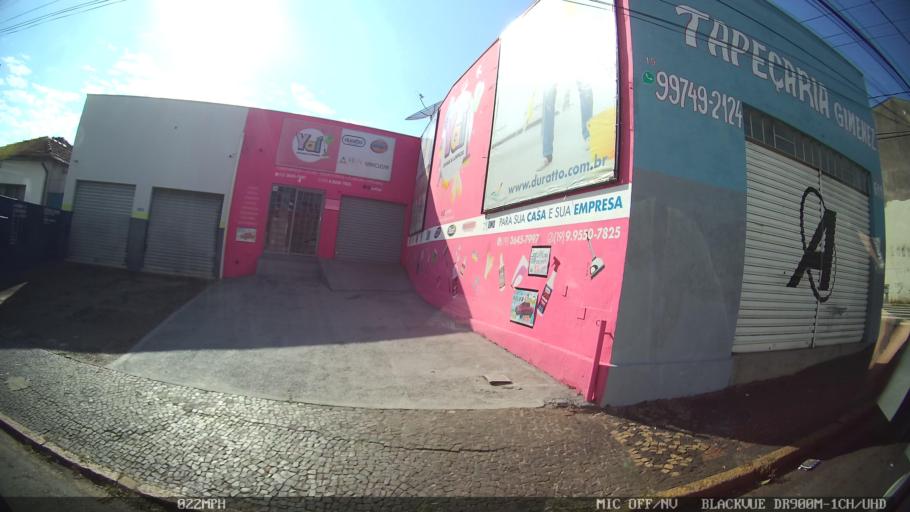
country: BR
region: Sao Paulo
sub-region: Americana
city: Americana
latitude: -22.7463
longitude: -47.3263
